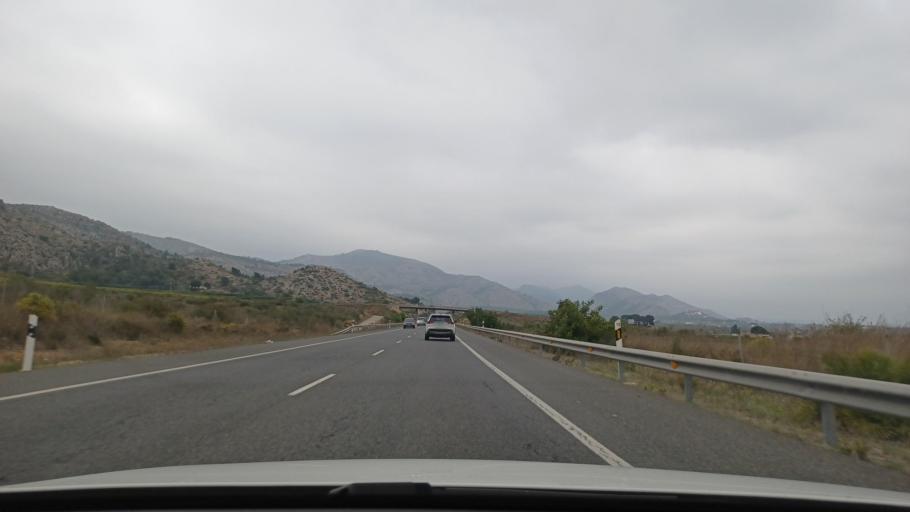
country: ES
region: Valencia
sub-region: Provincia de Castello
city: Borriol
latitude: 40.0197
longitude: -0.0415
